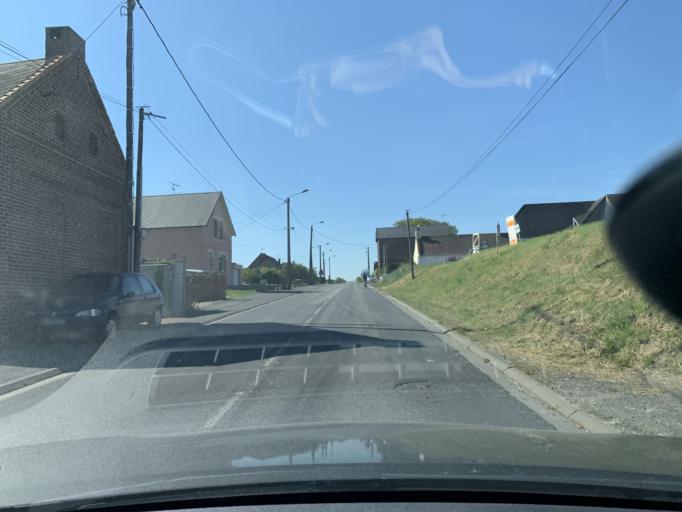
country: FR
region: Nord-Pas-de-Calais
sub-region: Departement du Nord
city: Cambrai
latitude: 50.1550
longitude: 3.2420
